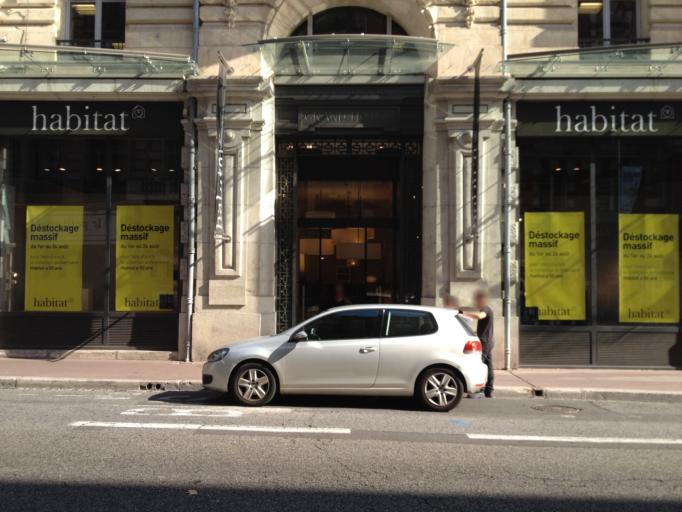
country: FR
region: Midi-Pyrenees
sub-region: Departement de la Haute-Garonne
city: Toulouse
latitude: 43.6006
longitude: 1.4487
